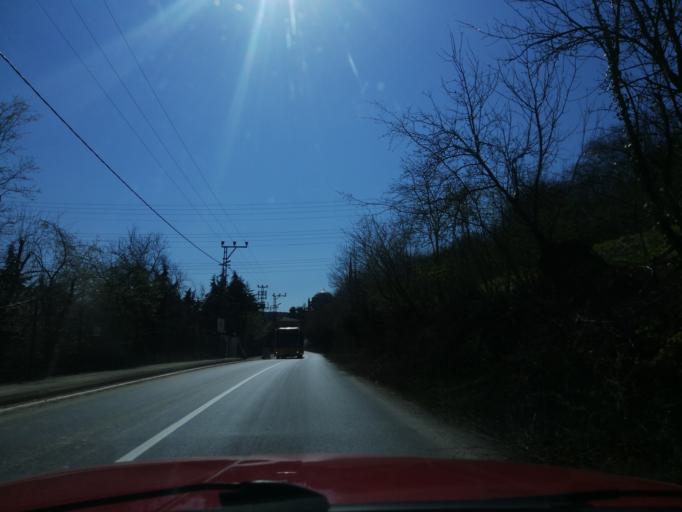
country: TR
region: Istanbul
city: Mahmut Sevket Pasa
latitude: 41.1300
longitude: 29.1617
